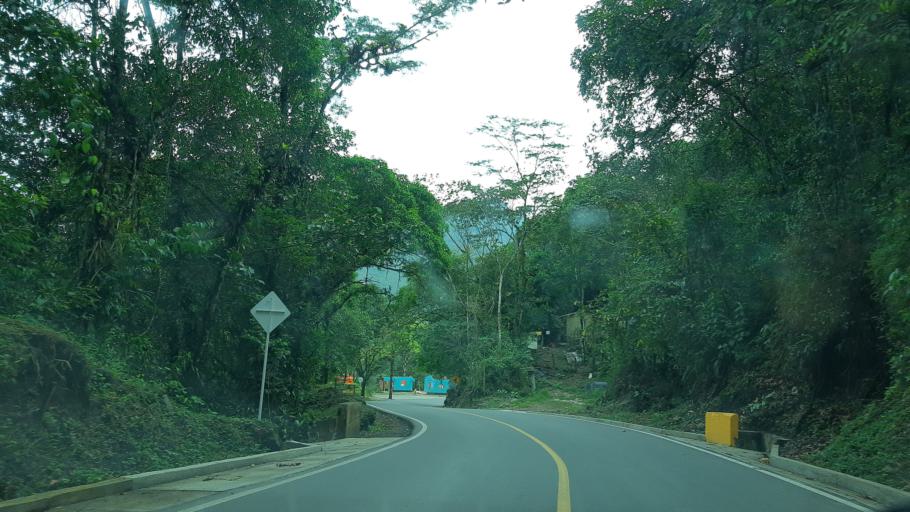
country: CO
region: Boyaca
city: Santa Maria
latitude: 4.8658
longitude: -73.2326
